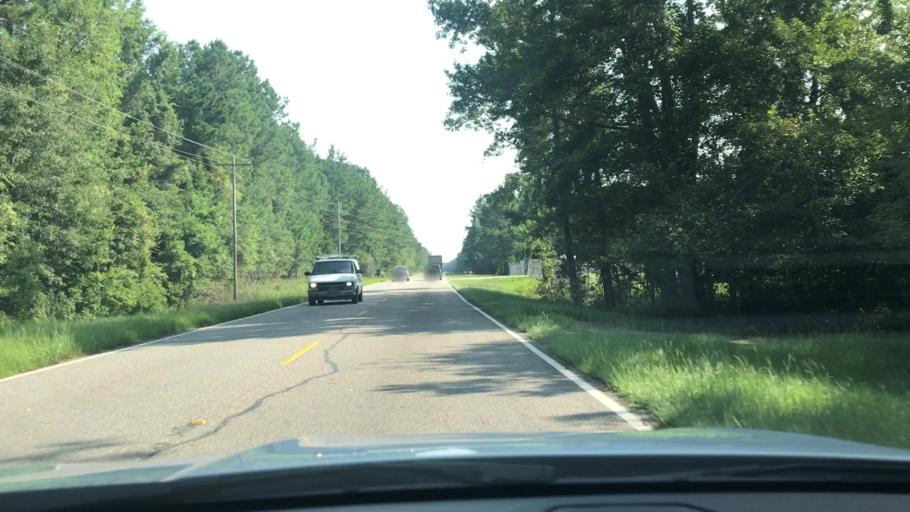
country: US
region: South Carolina
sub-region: Georgetown County
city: Georgetown
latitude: 33.4960
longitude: -79.2617
